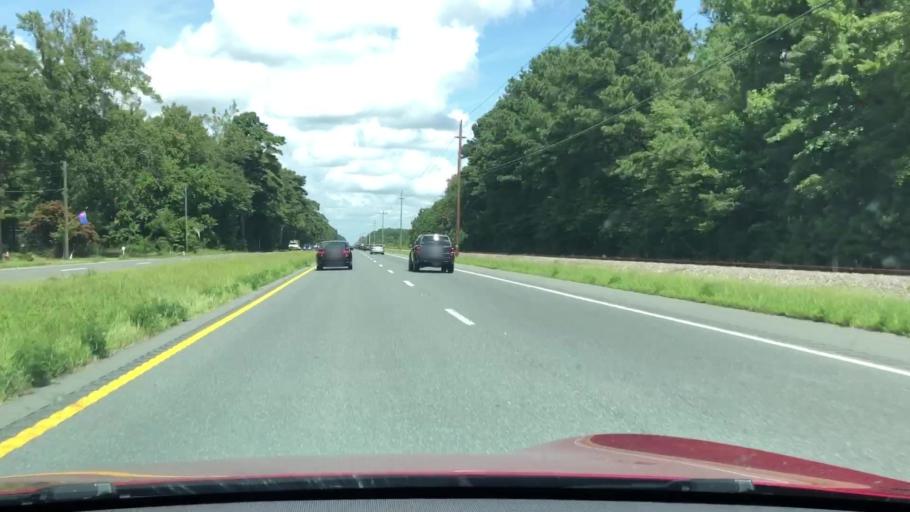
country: US
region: Virginia
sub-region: Northampton County
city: Eastville
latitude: 37.4312
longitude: -75.8875
